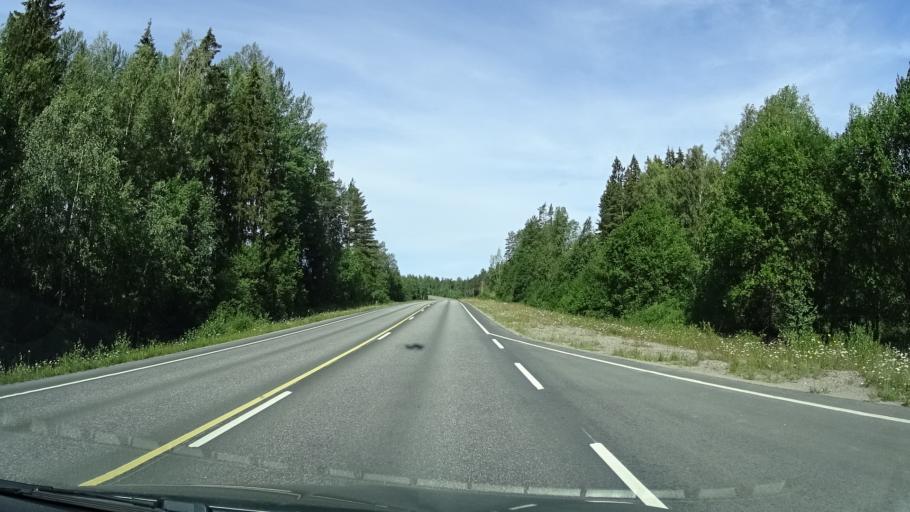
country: FI
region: Varsinais-Suomi
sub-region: Salo
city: Muurla
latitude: 60.3810
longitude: 23.2463
